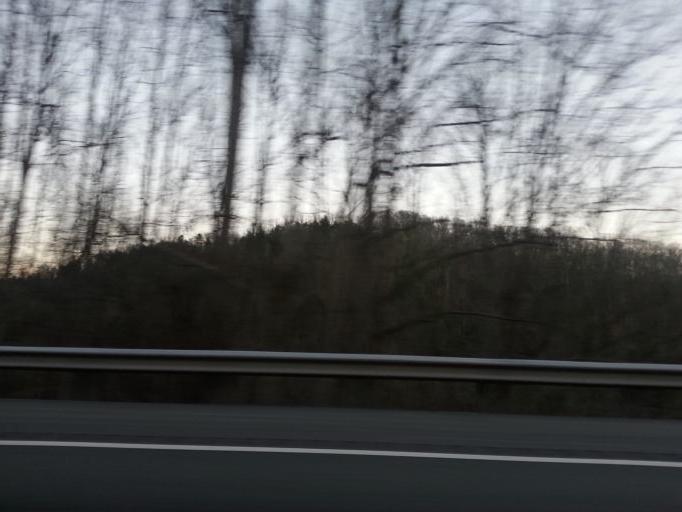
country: US
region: North Carolina
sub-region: Haywood County
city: Cove Creek
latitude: 35.6392
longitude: -82.9909
